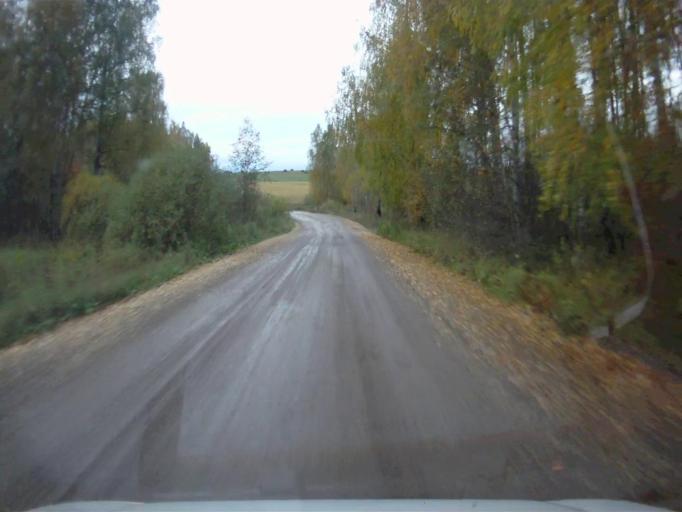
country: RU
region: Sverdlovsk
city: Mikhaylovsk
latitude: 56.1748
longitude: 59.2164
